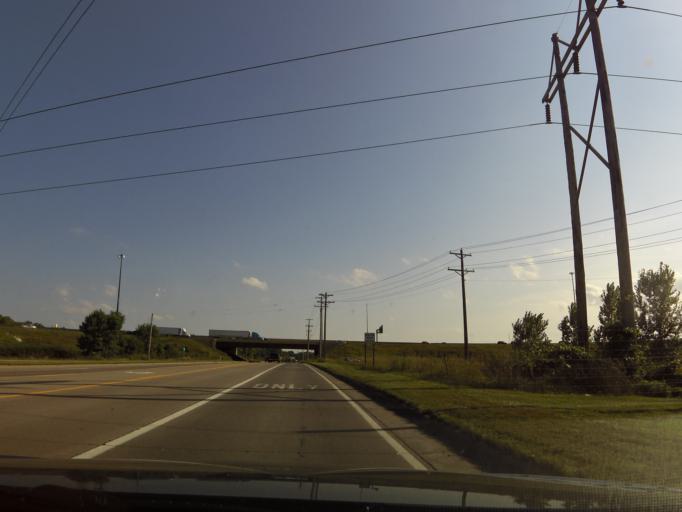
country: US
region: Minnesota
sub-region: Washington County
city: Newport
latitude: 44.8862
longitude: -93.0092
